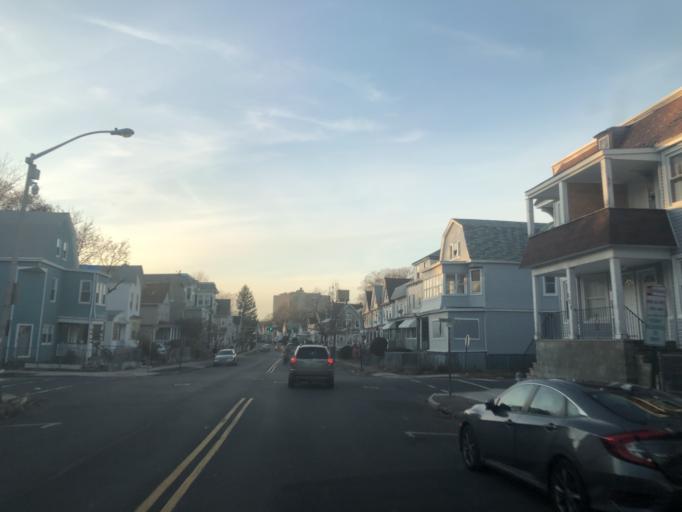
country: US
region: New Jersey
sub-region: Essex County
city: Orange
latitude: 40.7549
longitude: -74.2228
